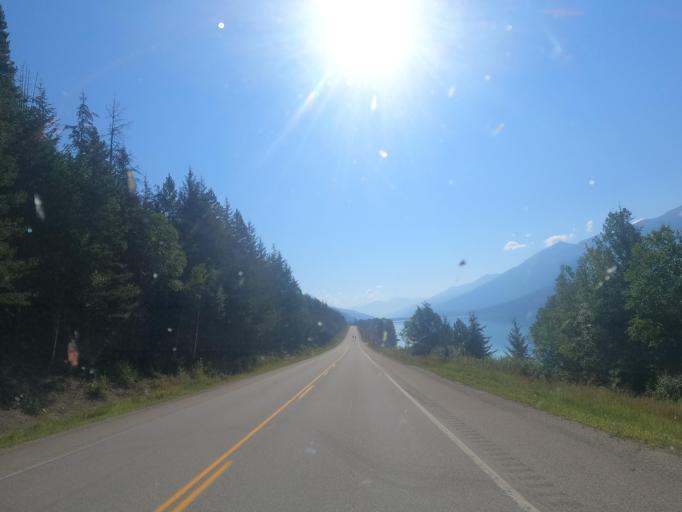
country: CA
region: Alberta
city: Jasper Park Lodge
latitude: 52.9610
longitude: -118.9076
